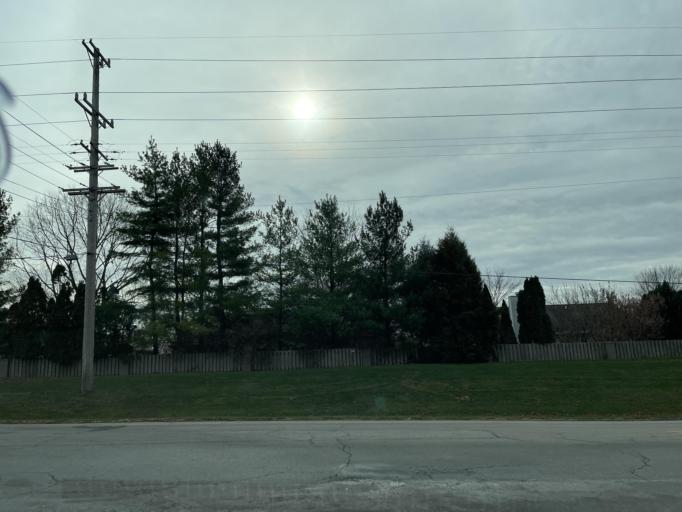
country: US
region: Illinois
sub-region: Sangamon County
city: Leland Grove
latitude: 39.7869
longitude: -89.7296
